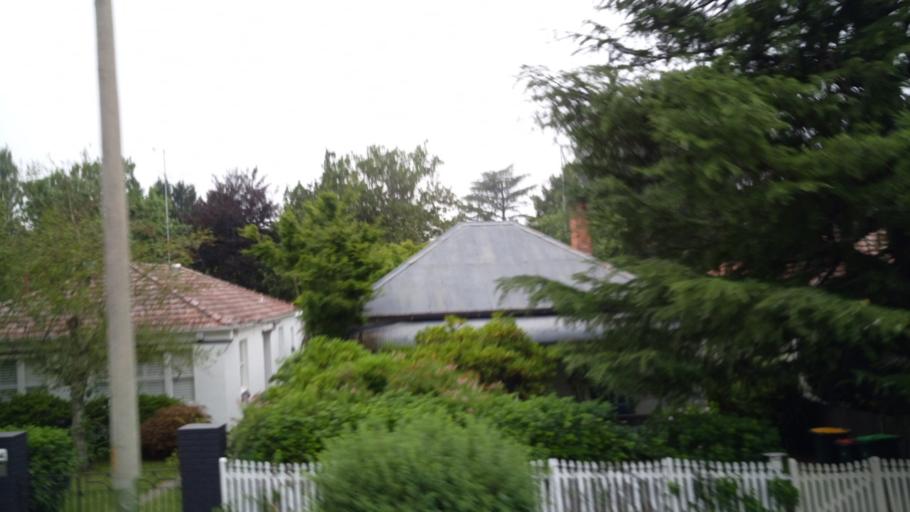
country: AU
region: New South Wales
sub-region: Blue Mountains Municipality
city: Leura
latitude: -33.7163
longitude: 150.3295
